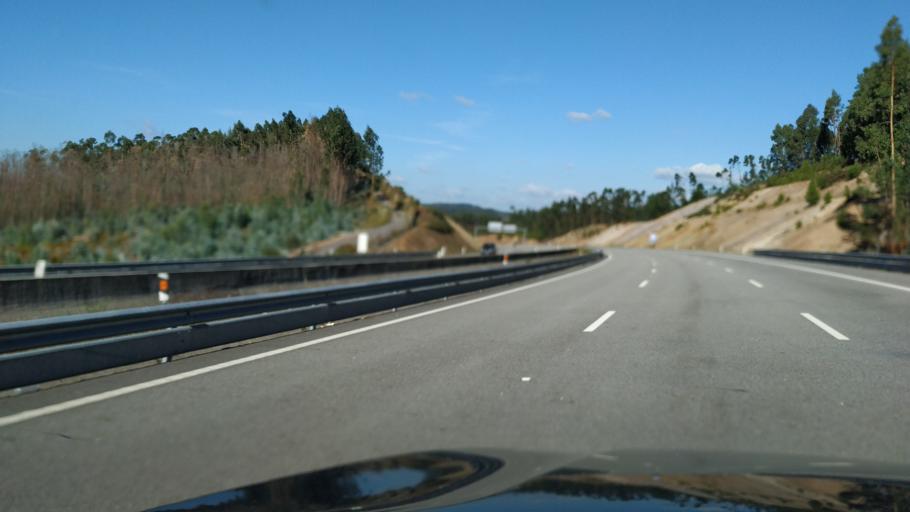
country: PT
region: Porto
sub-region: Vila Nova de Gaia
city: Sandim
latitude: 41.0257
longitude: -8.4788
